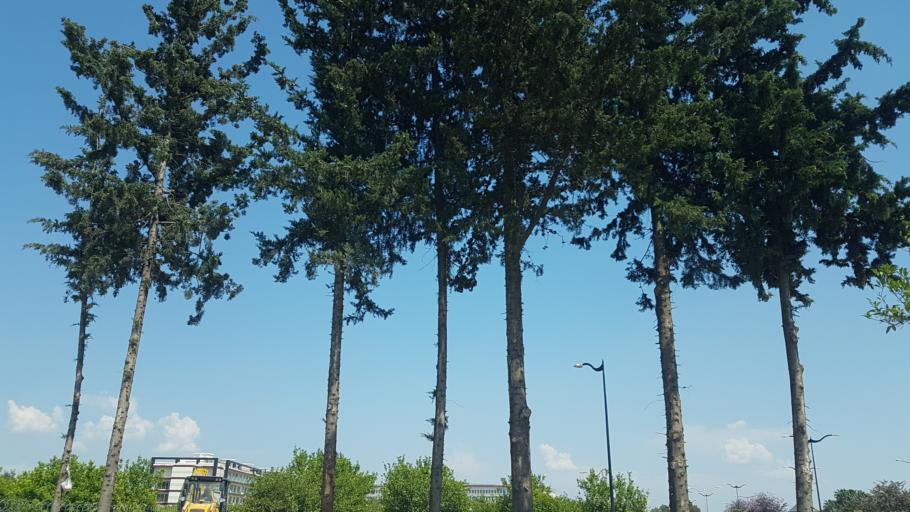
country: TR
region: Adana
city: Adana
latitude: 37.0098
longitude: 35.3373
